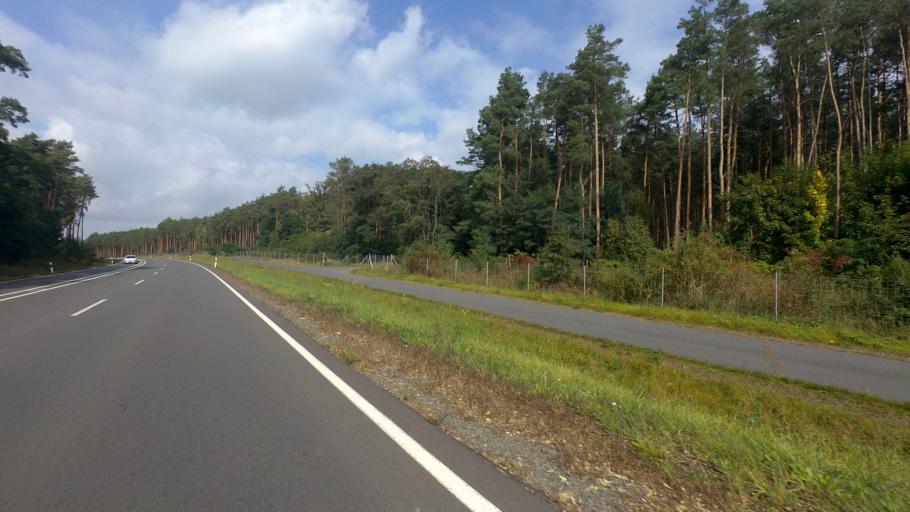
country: DE
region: Brandenburg
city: Falkenberg
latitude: 51.6432
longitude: 13.3041
